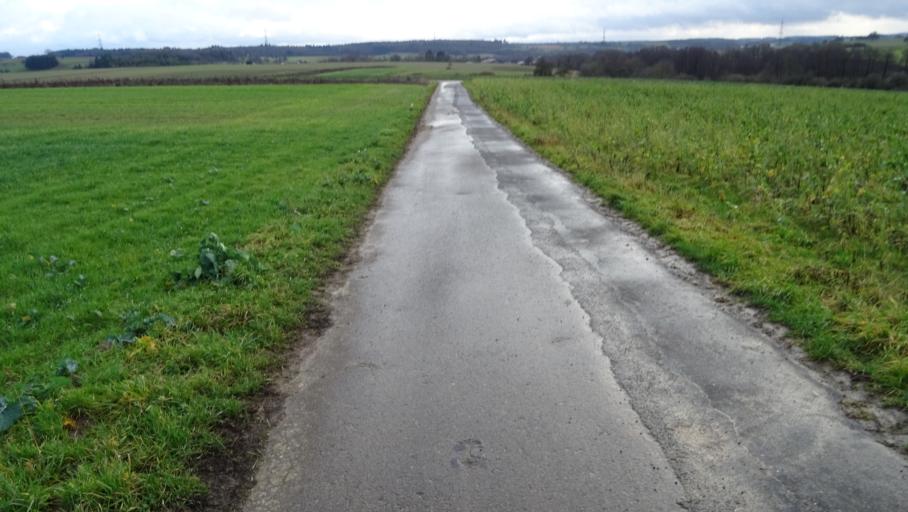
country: DE
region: Baden-Wuerttemberg
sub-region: Karlsruhe Region
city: Seckach
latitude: 49.4384
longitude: 9.2815
